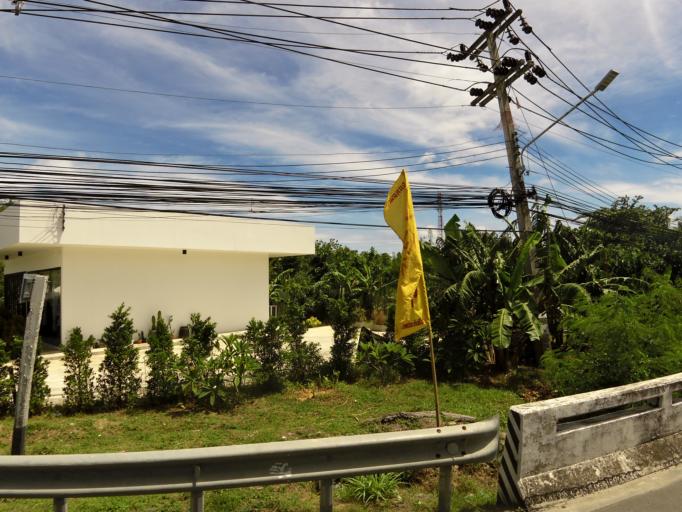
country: TH
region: Phuket
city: Ban Chalong
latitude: 7.8499
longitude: 98.3344
